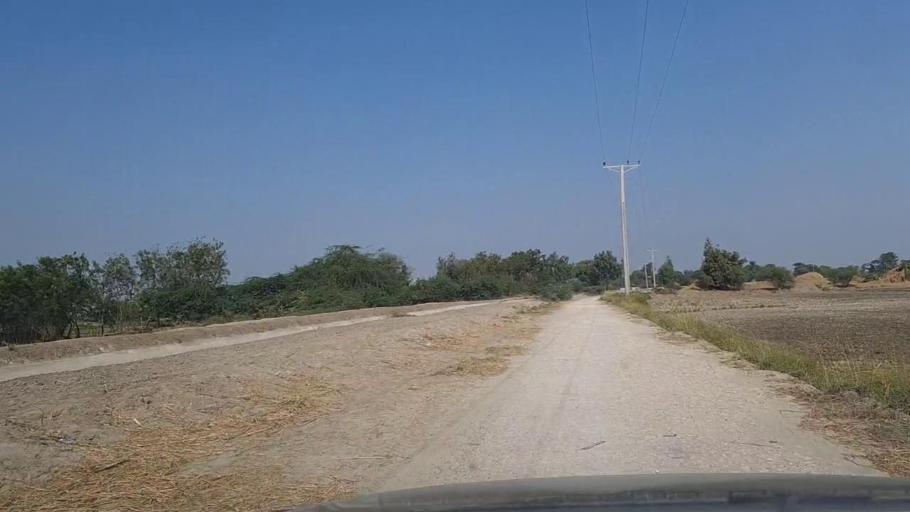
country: PK
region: Sindh
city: Mirpur Sakro
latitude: 24.5167
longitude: 67.8052
